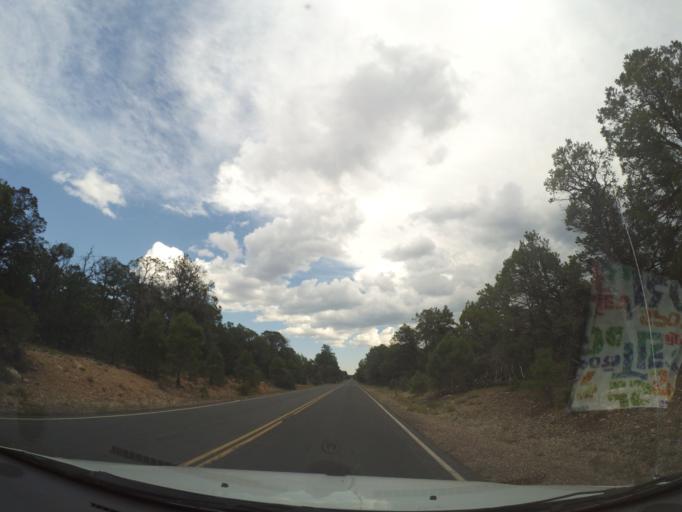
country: US
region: Arizona
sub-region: Coconino County
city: Grand Canyon
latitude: 36.0063
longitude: -112.0473
